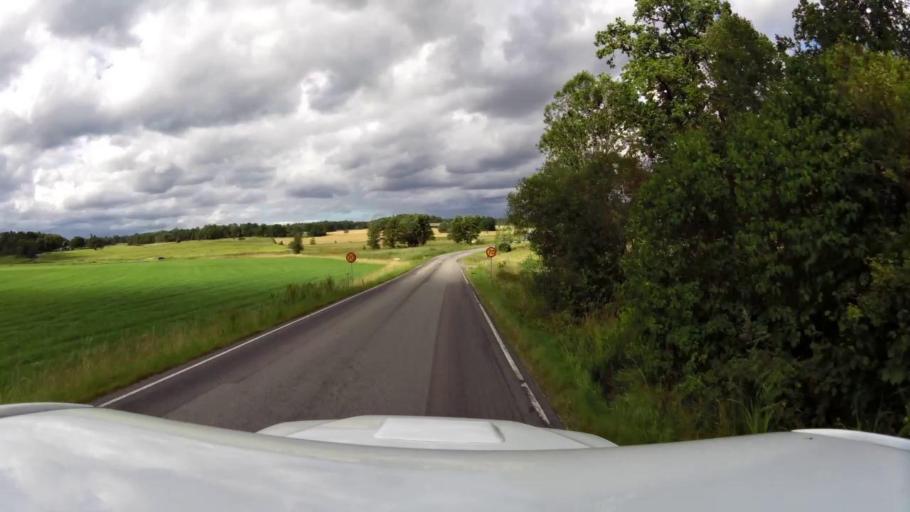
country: SE
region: OEstergoetland
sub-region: Linkopings Kommun
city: Sturefors
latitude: 58.3275
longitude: 15.7142
